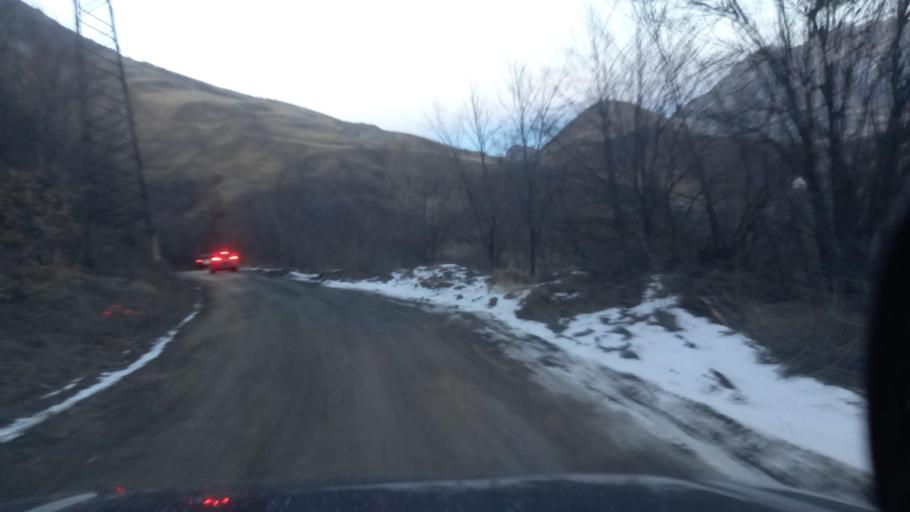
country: RU
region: Ingushetiya
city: Dzhayrakh
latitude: 42.8282
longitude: 44.5834
